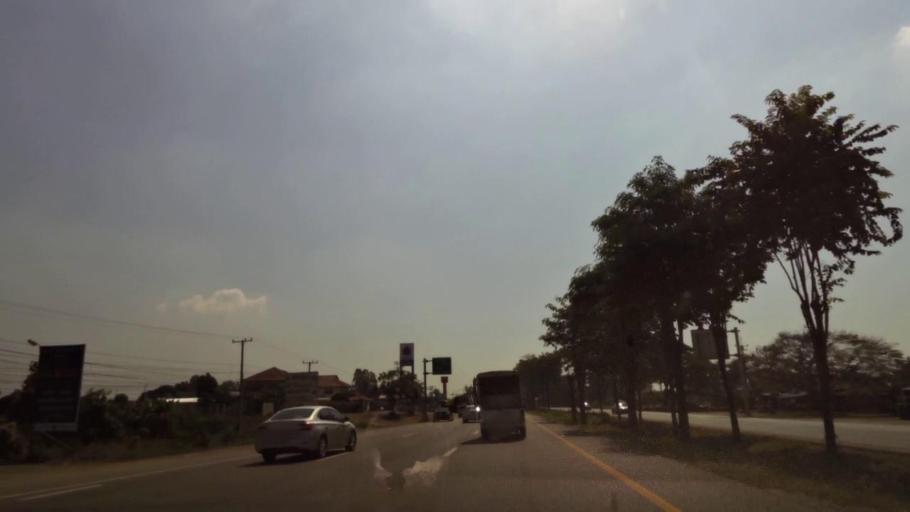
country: TH
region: Phichit
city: Bueng Na Rang
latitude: 16.1200
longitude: 100.1257
